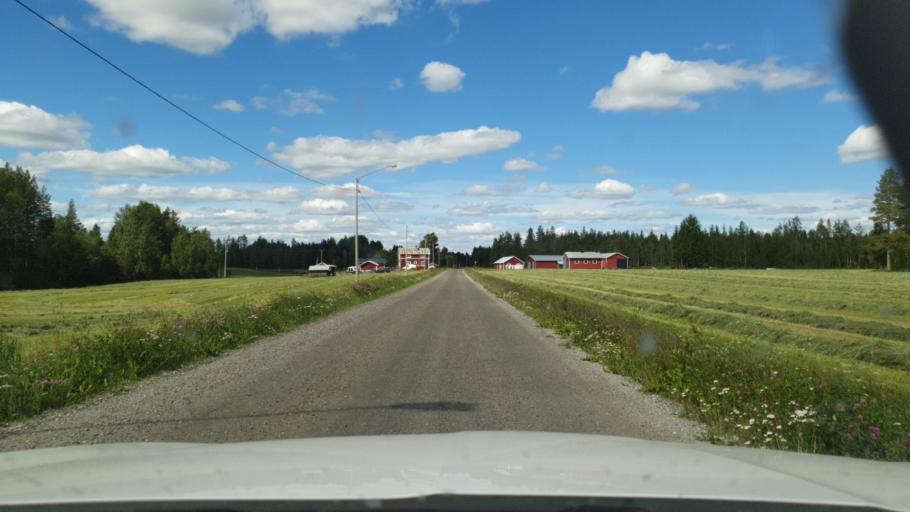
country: SE
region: Vaesterbotten
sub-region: Skelleftea Kommun
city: Backa
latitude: 65.1827
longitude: 21.0688
